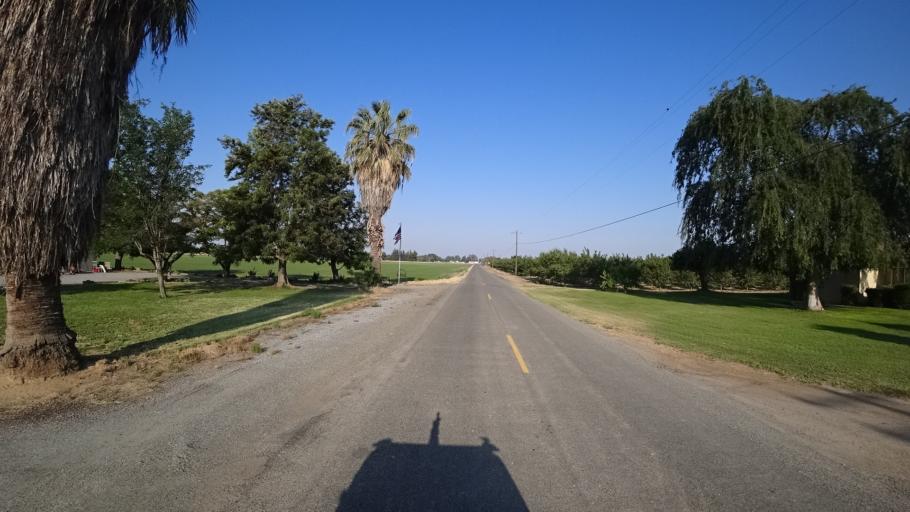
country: US
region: California
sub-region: Kings County
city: Lemoore
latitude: 36.3730
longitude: -119.8042
